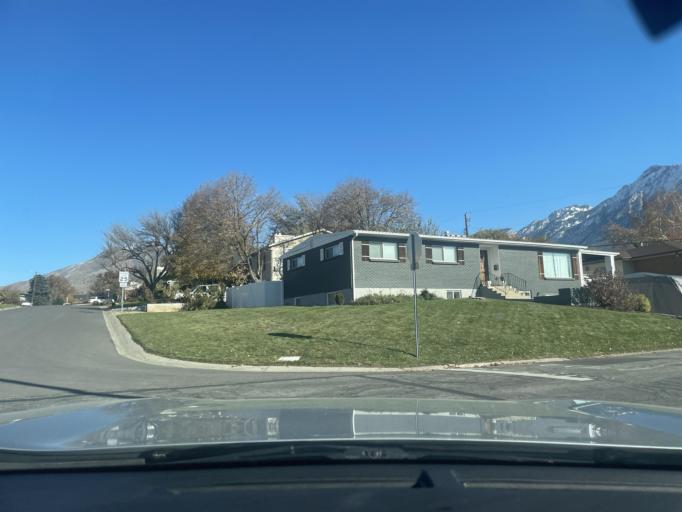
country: US
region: Utah
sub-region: Salt Lake County
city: Holladay
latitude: 40.6782
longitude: -111.8303
